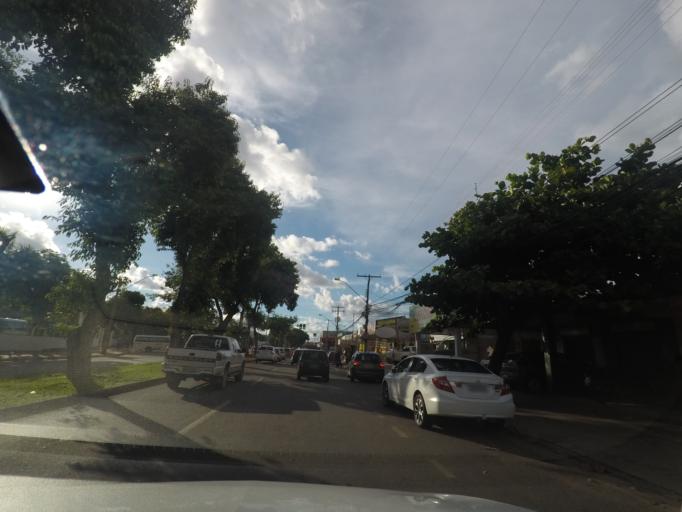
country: BR
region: Goias
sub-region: Goiania
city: Goiania
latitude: -16.6814
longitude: -49.3071
